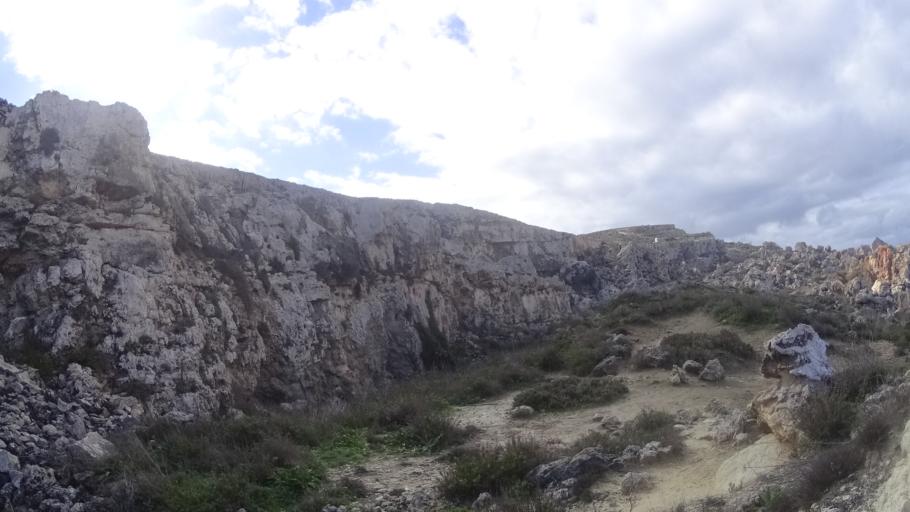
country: MT
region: Il-Mellieha
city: Mellieha
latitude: 35.9800
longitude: 14.3288
